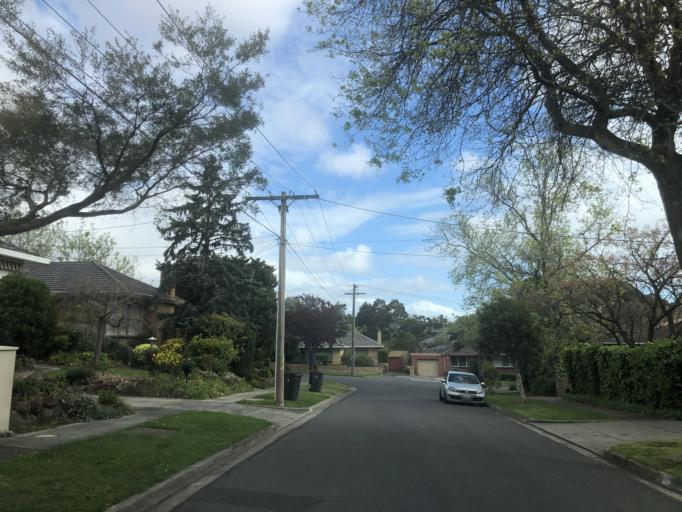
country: AU
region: Victoria
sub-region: Monash
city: Ashwood
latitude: -37.8824
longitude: 145.1195
